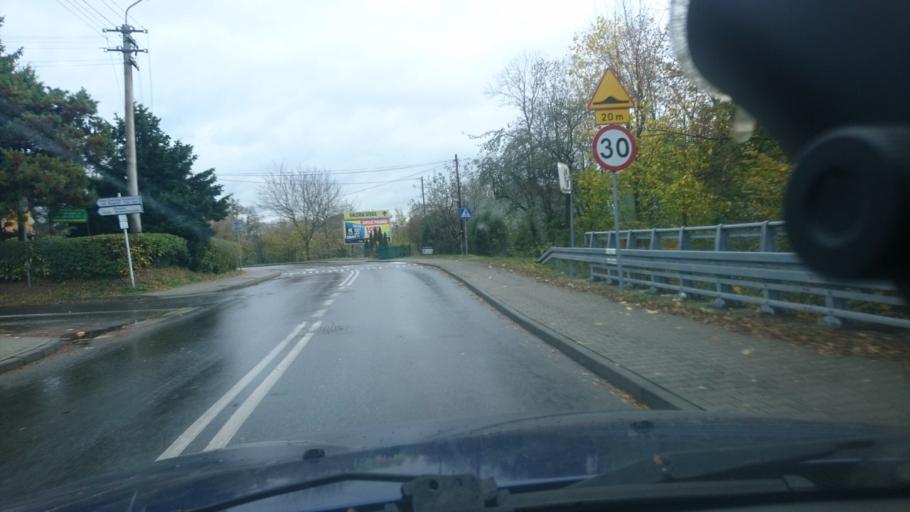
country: PL
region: Silesian Voivodeship
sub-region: Bielsko-Biala
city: Bielsko-Biala
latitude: 49.8263
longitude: 19.0178
